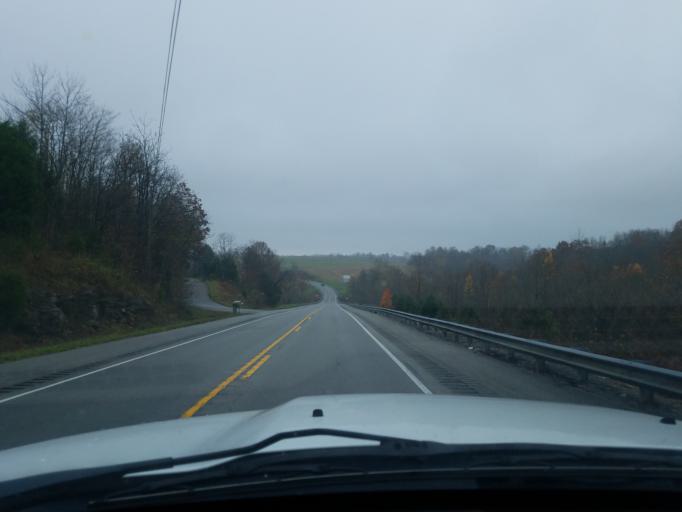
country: US
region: Kentucky
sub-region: Green County
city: Greensburg
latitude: 37.3978
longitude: -85.4717
